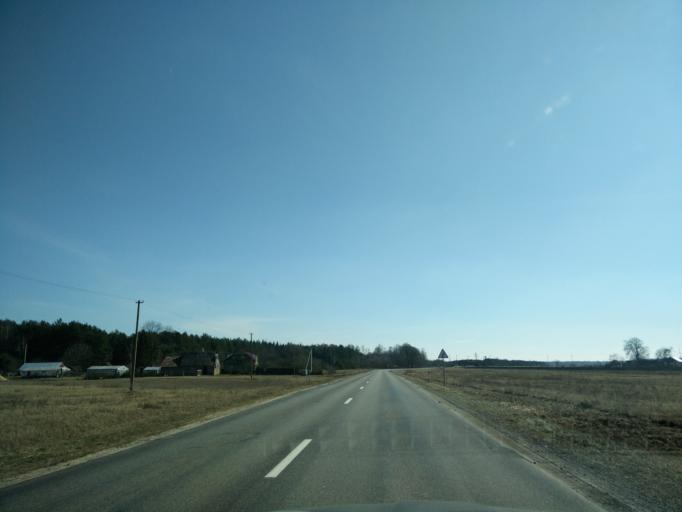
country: LT
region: Klaipedos apskritis
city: Silute
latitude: 55.3297
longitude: 21.5192
